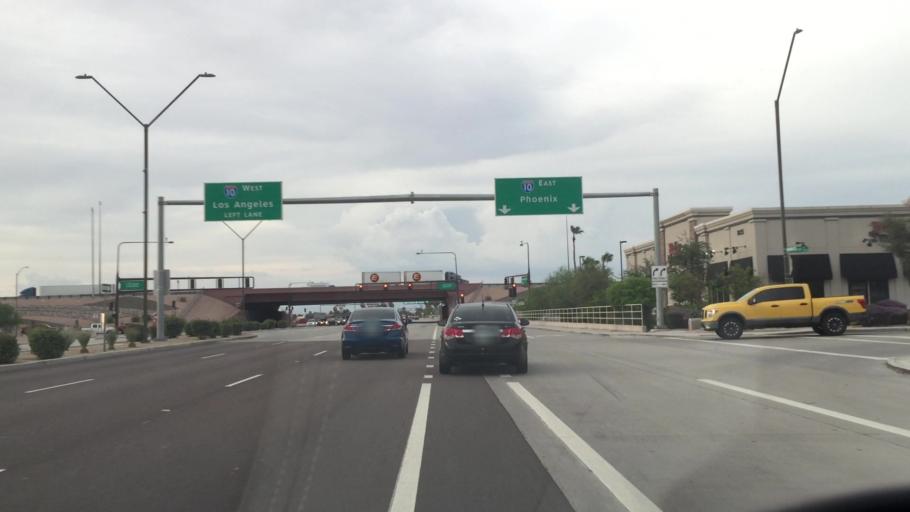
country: US
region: Arizona
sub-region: Maricopa County
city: Tolleson
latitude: 33.4574
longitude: -112.3064
